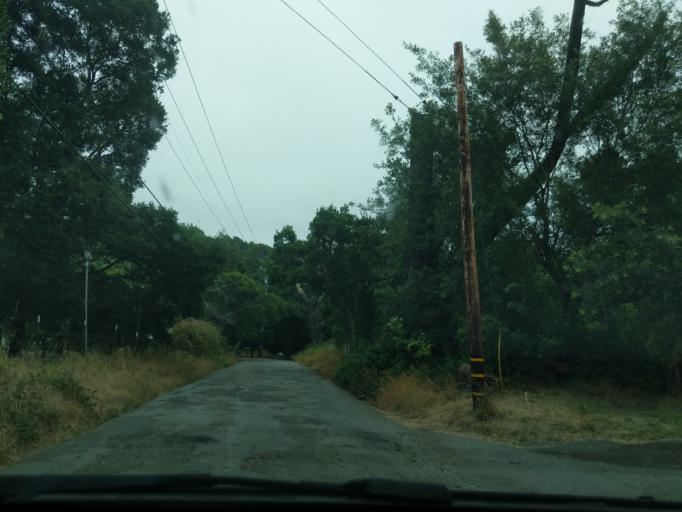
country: US
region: California
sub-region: San Benito County
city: Aromas
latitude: 36.8751
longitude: -121.6222
